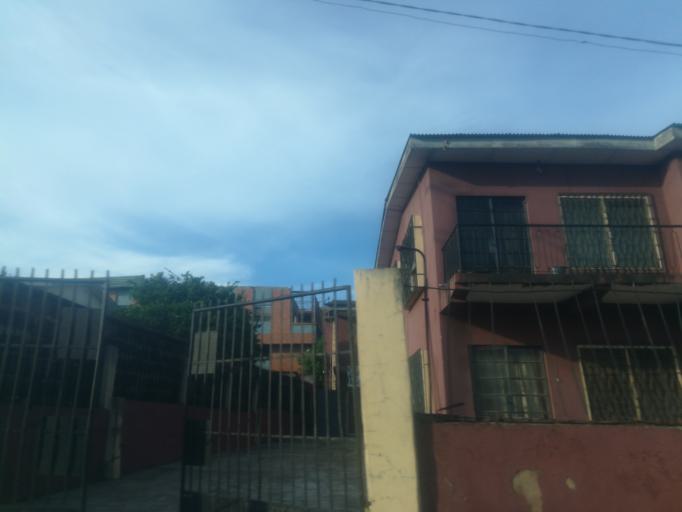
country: NG
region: Oyo
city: Ibadan
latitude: 7.3431
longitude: 3.8896
